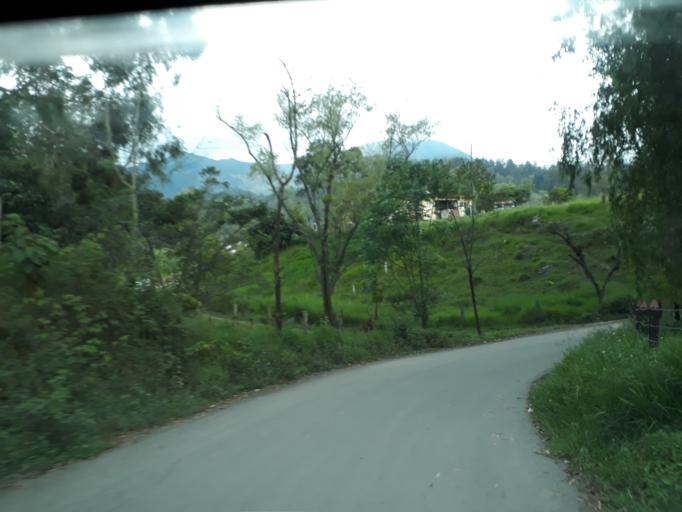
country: CO
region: Cundinamarca
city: Pacho
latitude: 5.1629
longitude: -74.1245
